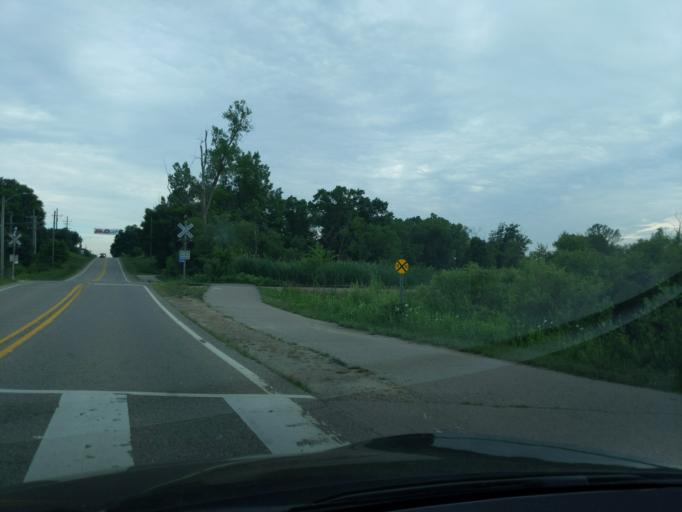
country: US
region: Michigan
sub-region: Livingston County
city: Whitmore Lake
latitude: 42.4539
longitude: -83.8215
